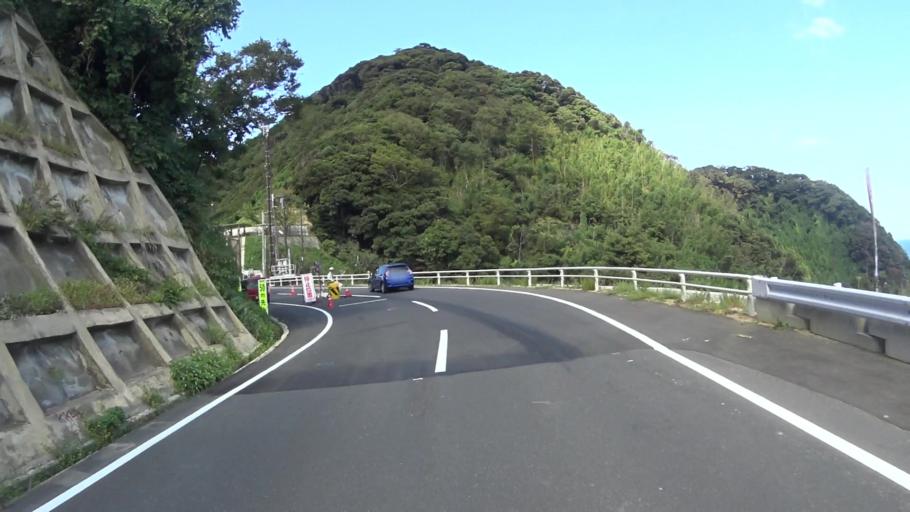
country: JP
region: Kyoto
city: Miyazu
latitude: 35.7553
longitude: 135.2508
